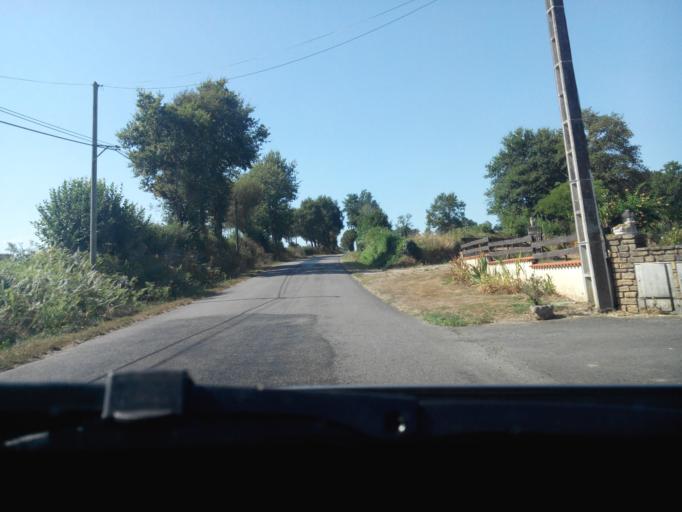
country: FR
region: Poitou-Charentes
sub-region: Departement de la Charente
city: Etagnac
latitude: 45.9422
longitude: 0.7752
